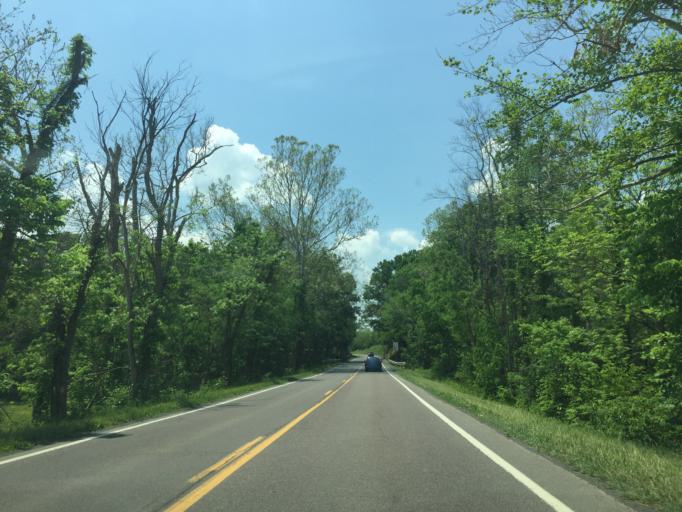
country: US
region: Virginia
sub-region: Shenandoah County
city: Woodstock
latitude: 39.0892
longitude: -78.5820
